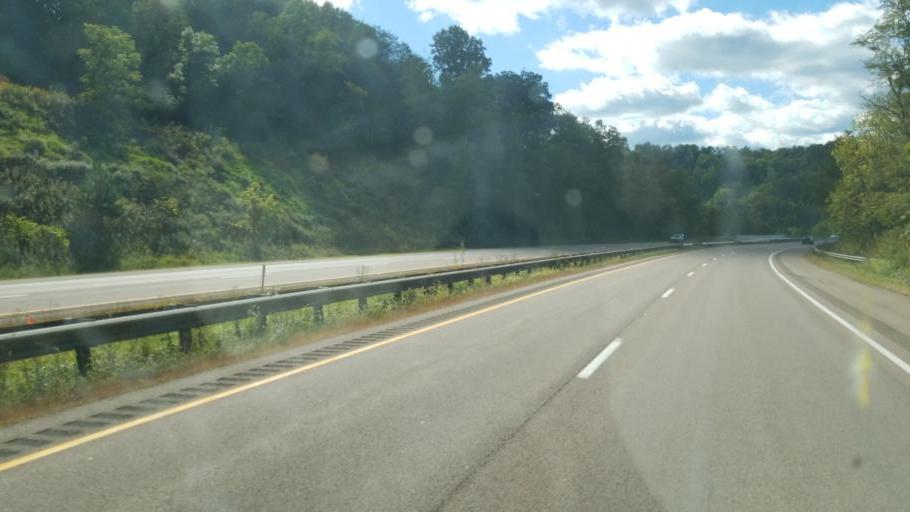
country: US
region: Maryland
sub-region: Garrett County
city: Oakland
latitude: 39.6610
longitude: -79.4033
